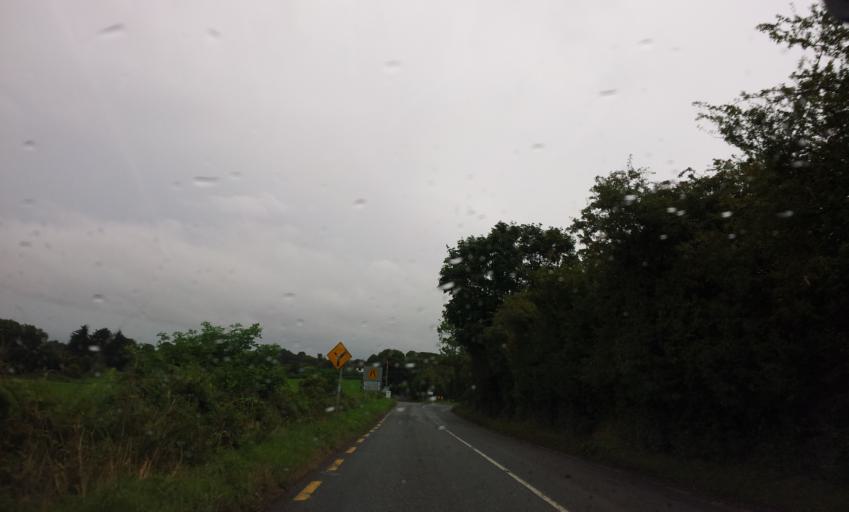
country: IE
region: Munster
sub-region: County Cork
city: Mallow
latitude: 52.2371
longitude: -8.4769
